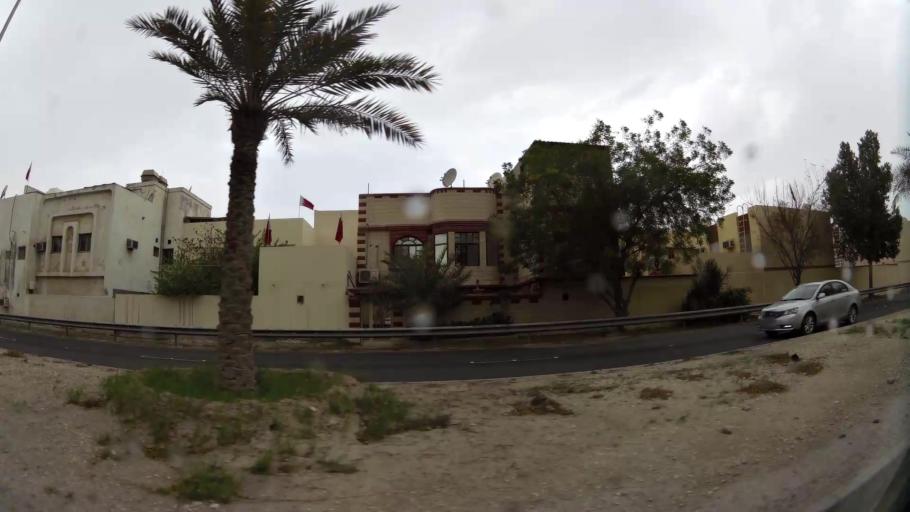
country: BH
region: Northern
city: Ar Rifa'
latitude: 26.1403
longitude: 50.5616
